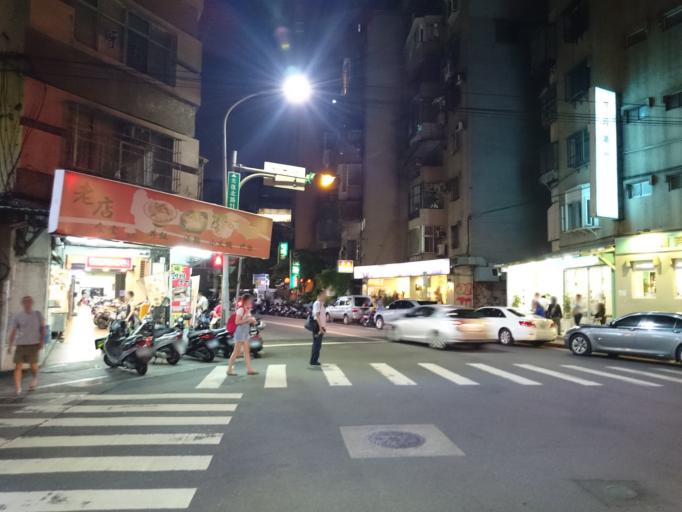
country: TW
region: Taipei
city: Taipei
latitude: 25.0501
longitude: 121.5608
